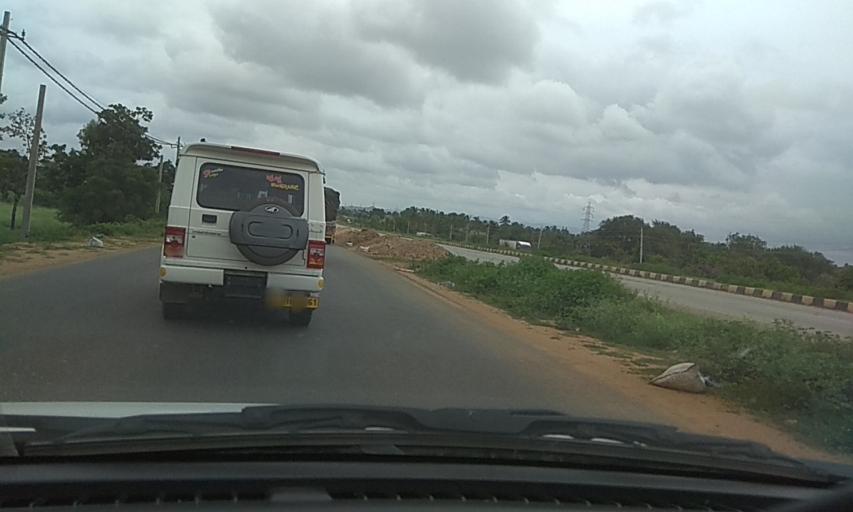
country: IN
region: Karnataka
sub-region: Chitradurga
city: Chitradurga
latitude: 14.2921
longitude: 76.2839
